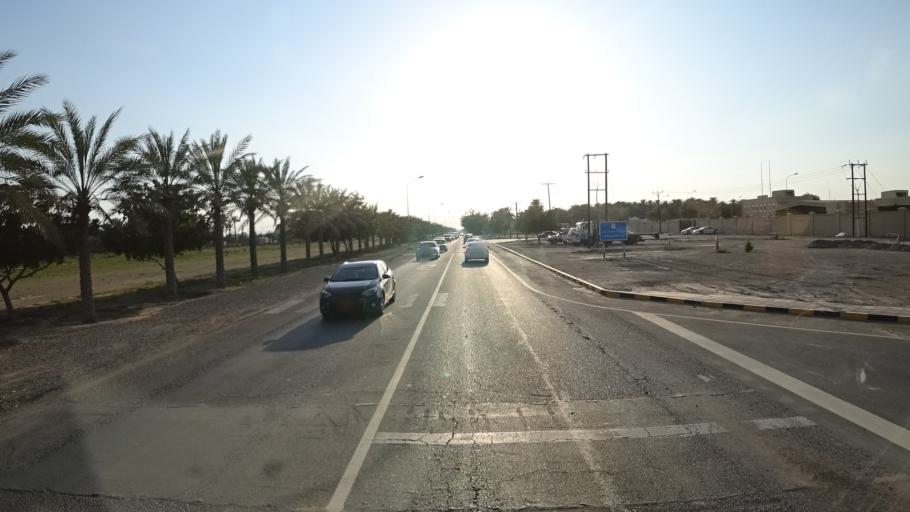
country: OM
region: Al Batinah
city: Al Khaburah
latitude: 23.9673
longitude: 57.0850
